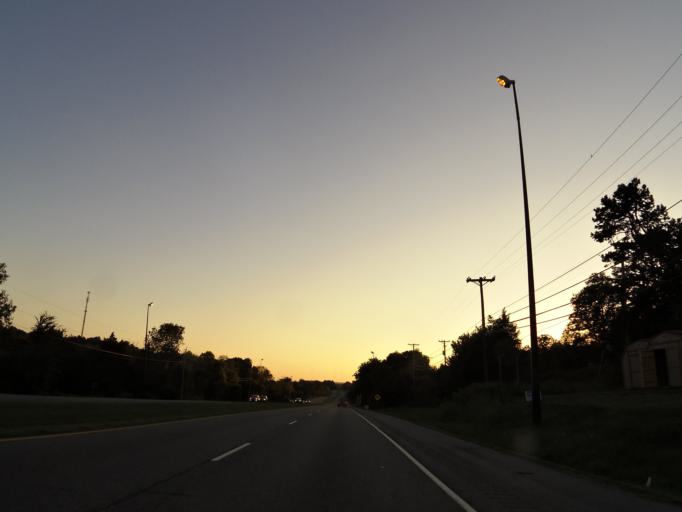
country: US
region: Tennessee
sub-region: Knox County
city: Mascot
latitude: 36.0198
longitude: -83.7953
